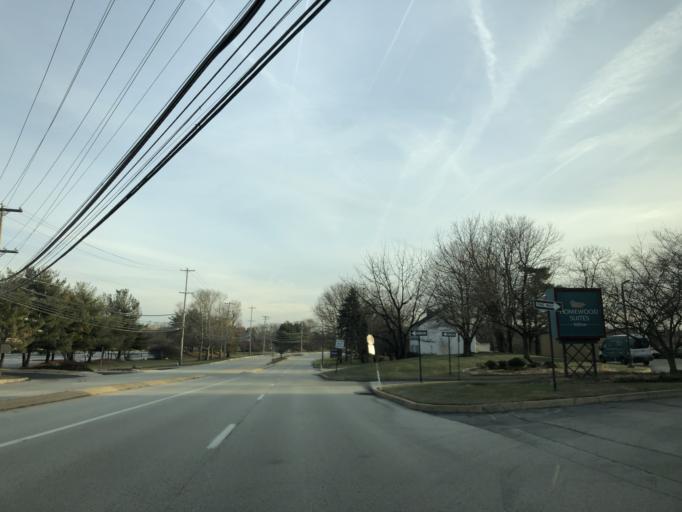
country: US
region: Pennsylvania
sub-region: Chester County
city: Malvern
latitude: 40.0532
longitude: -75.5256
